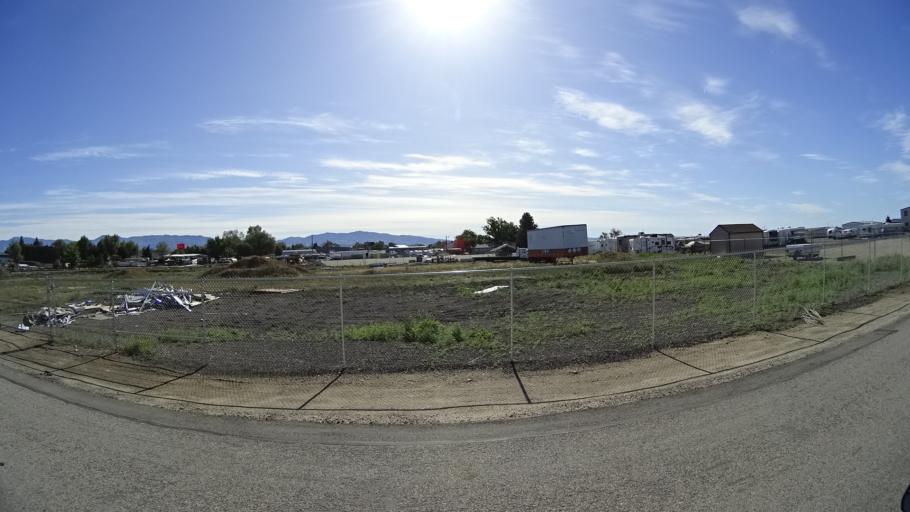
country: US
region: Idaho
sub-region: Ada County
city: Garden City
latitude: 43.5801
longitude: -116.2611
